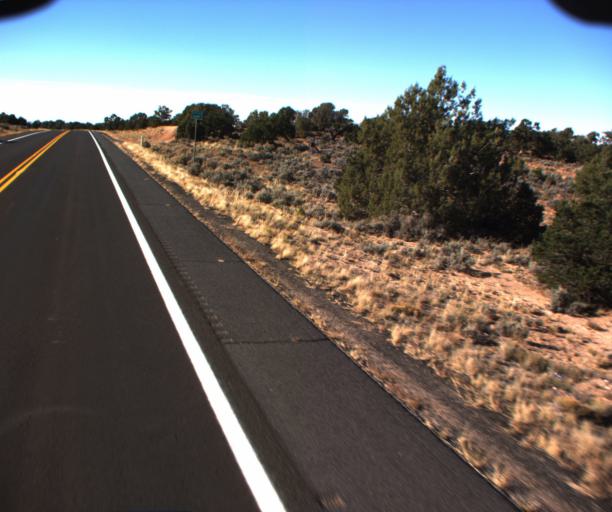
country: US
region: Arizona
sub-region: Coconino County
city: Kaibito
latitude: 36.5865
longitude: -110.8699
